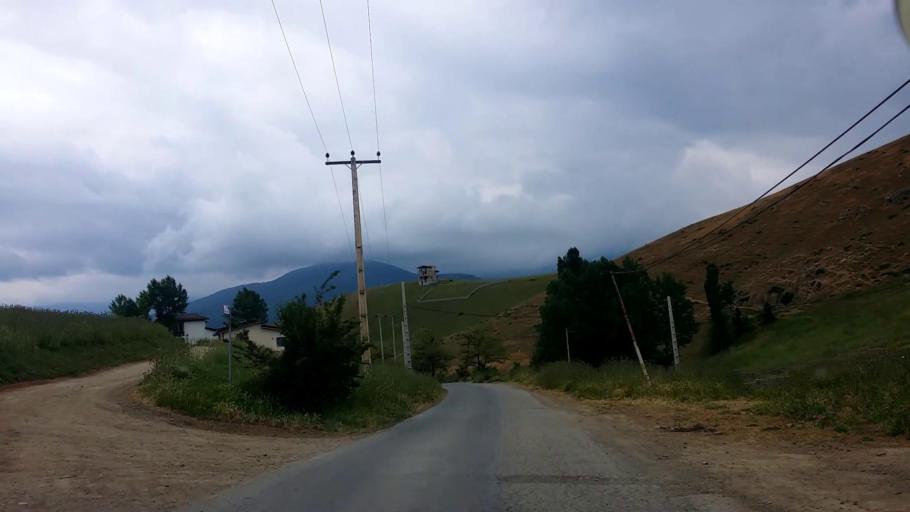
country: IR
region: Mazandaran
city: Chalus
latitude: 36.5216
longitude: 51.2614
